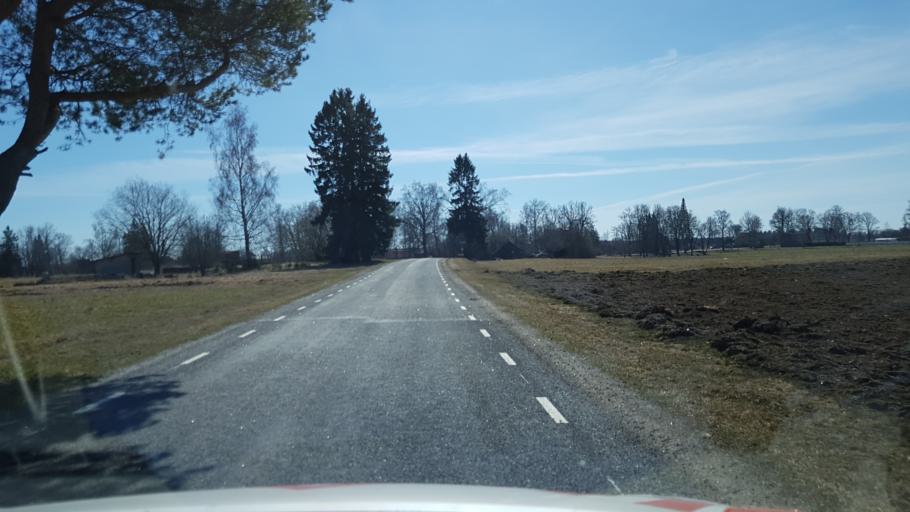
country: EE
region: Laeaene-Virumaa
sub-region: Vinni vald
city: Vinni
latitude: 59.1016
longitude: 26.5263
